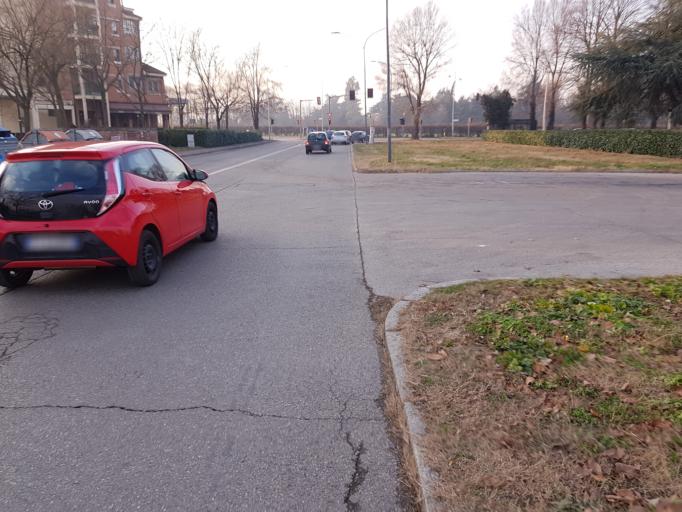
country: IT
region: Emilia-Romagna
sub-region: Provincia di Bologna
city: Quarto Inferiore
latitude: 44.5123
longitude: 11.3874
